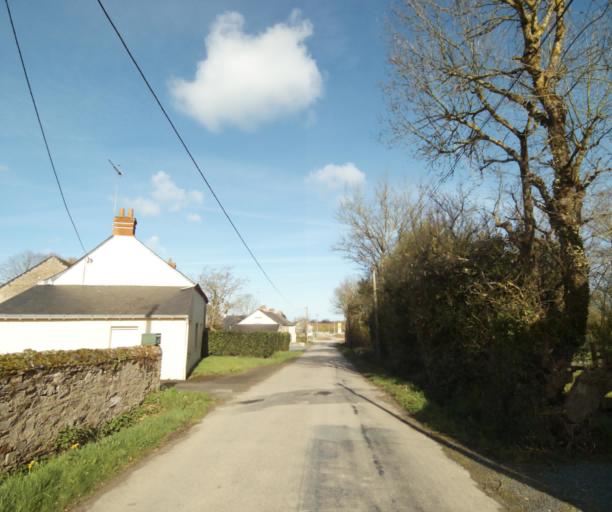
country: FR
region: Pays de la Loire
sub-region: Departement de la Loire-Atlantique
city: Bouvron
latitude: 47.4092
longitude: -1.8420
